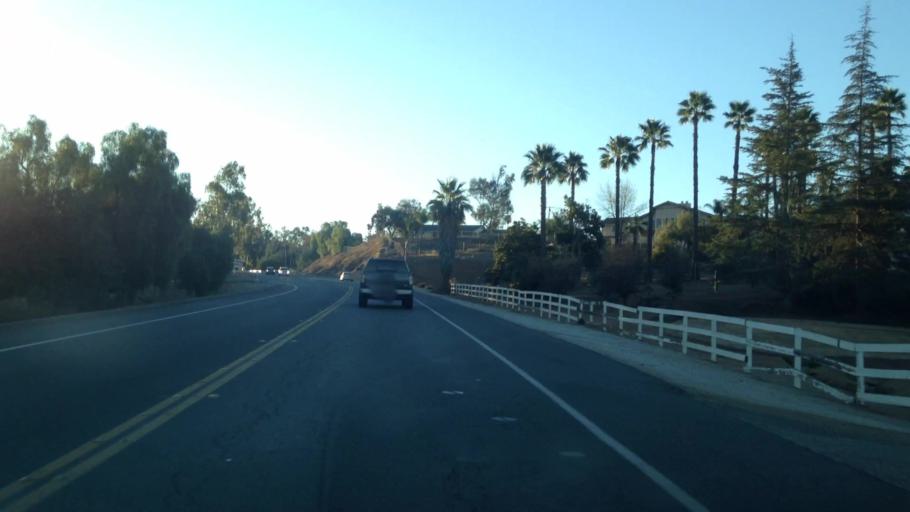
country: US
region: California
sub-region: Riverside County
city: Woodcrest
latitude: 33.8988
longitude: -117.3823
